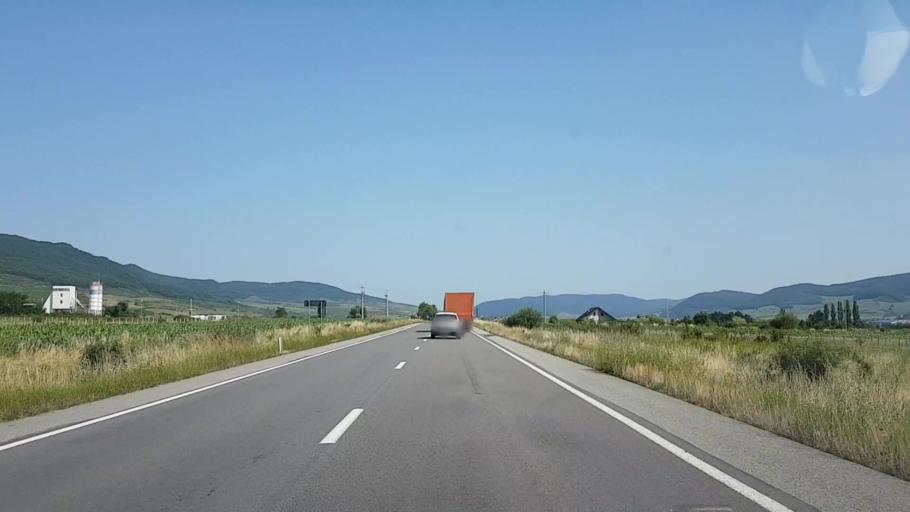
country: RO
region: Bistrita-Nasaud
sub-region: Comuna Sieu-Magherus
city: Sieu-Magherus
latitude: 47.1090
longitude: 24.3473
